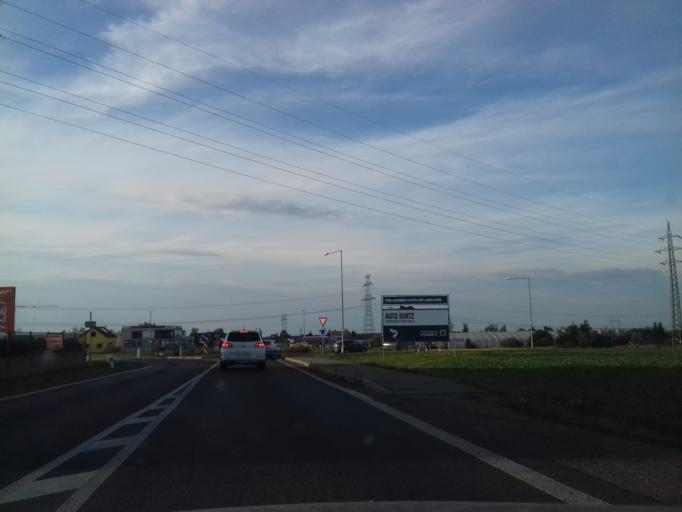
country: CZ
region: Central Bohemia
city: Vestec
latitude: 49.9903
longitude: 14.4908
